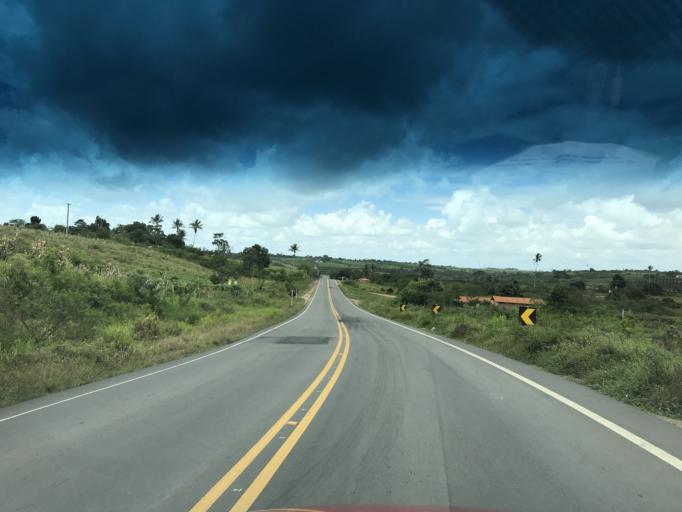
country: BR
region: Bahia
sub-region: Conceicao Do Almeida
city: Conceicao do Almeida
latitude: -12.7032
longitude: -39.2358
